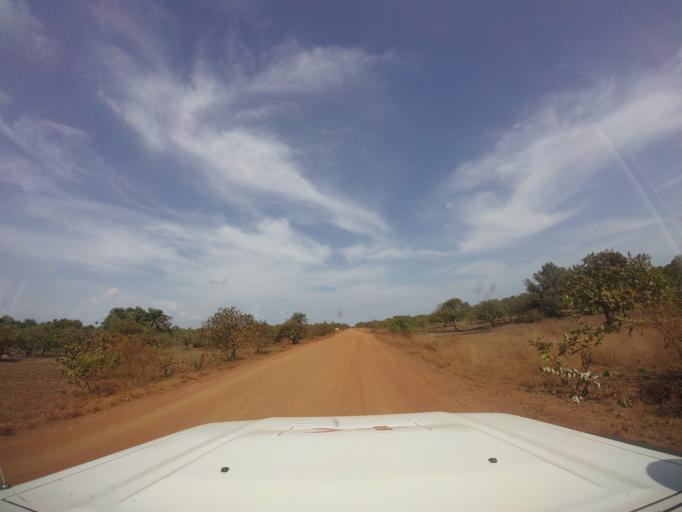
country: LR
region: Grand Cape Mount
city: Robertsport
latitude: 6.6919
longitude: -11.2766
